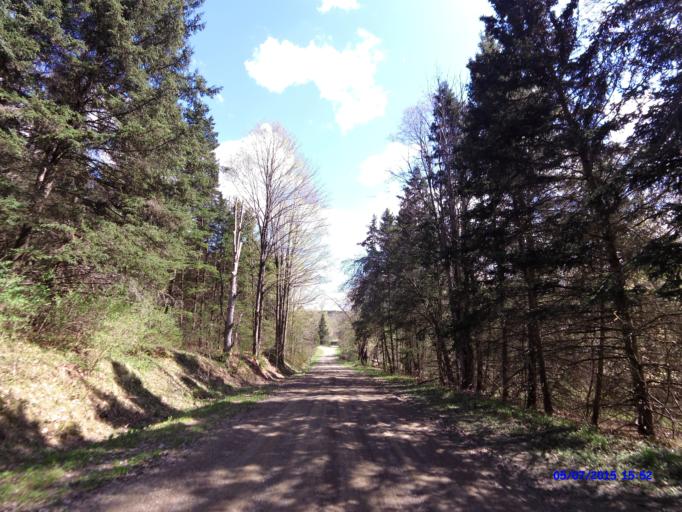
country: US
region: New York
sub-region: Cattaraugus County
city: Franklinville
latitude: 42.3262
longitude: -78.5420
